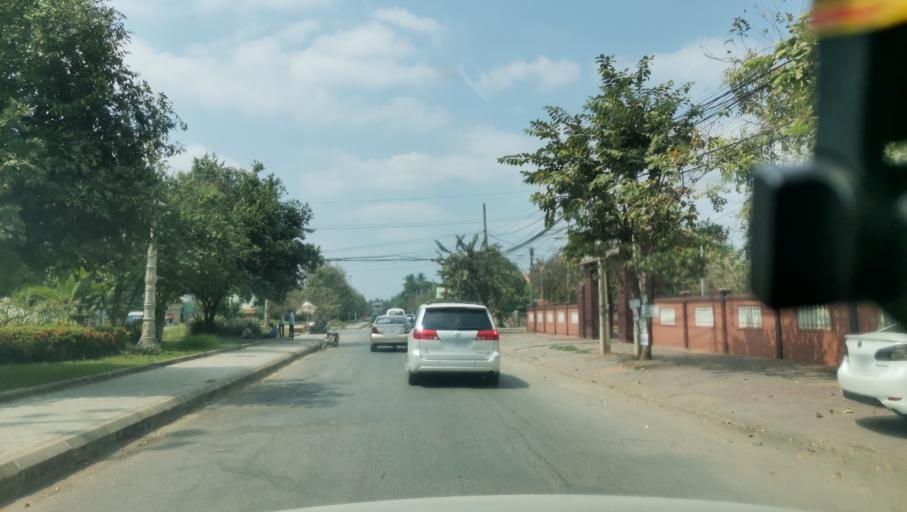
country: KH
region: Battambang
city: Battambang
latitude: 13.1076
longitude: 103.1991
